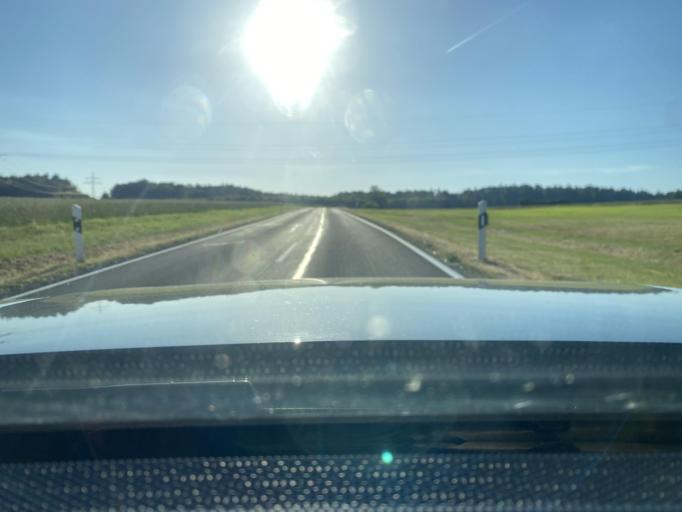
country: DE
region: Bavaria
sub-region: Regierungsbezirk Unterfranken
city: Roden
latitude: 49.9026
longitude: 9.6124
